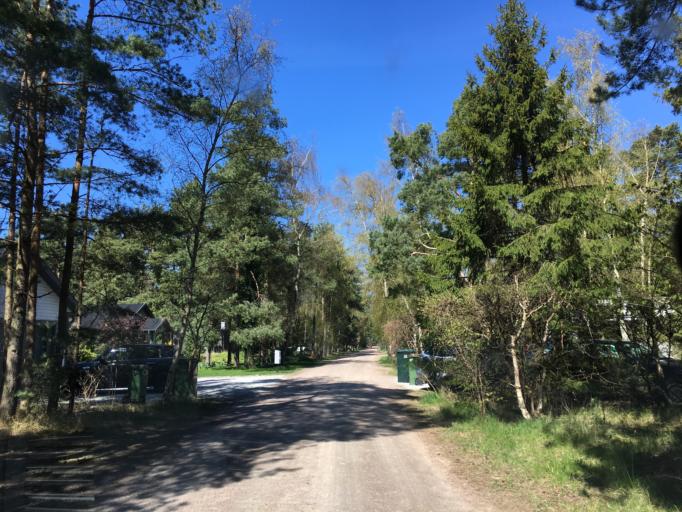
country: SE
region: Skane
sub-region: Vellinge Kommun
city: Ljunghusen
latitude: 55.3986
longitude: 12.9305
